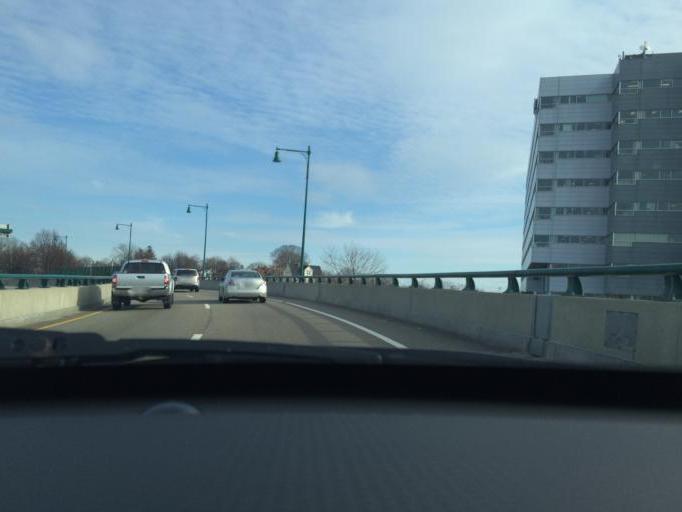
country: US
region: Massachusetts
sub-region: Norfolk County
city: Quincy
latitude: 42.2819
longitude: -71.0358
